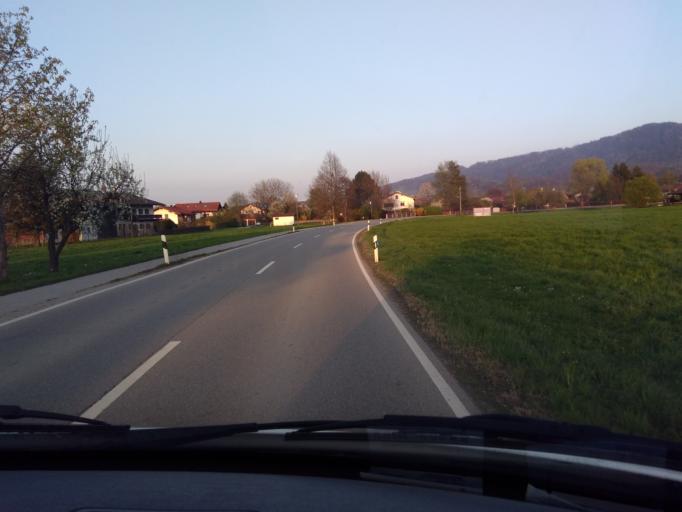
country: DE
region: Bavaria
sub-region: Upper Bavaria
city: Altenmarkt
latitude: 47.7825
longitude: 12.1304
